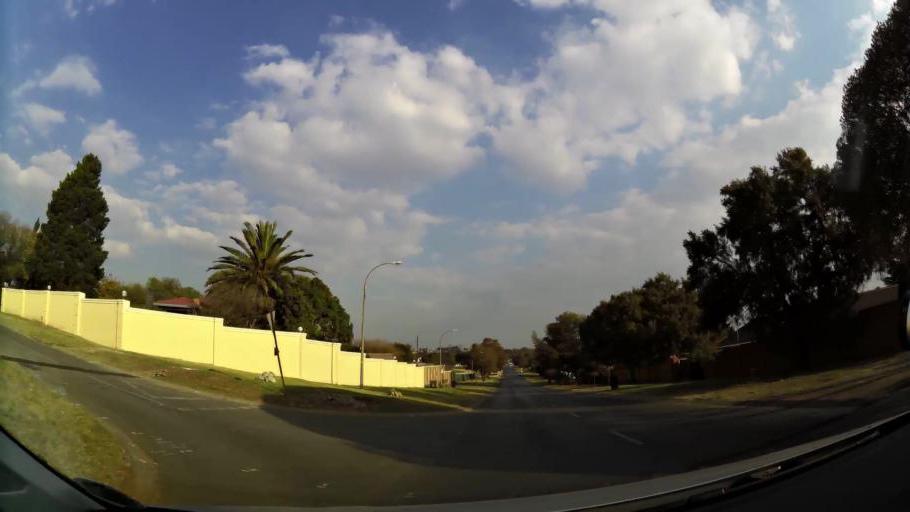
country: ZA
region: Gauteng
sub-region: City of Johannesburg Metropolitan Municipality
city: Modderfontein
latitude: -26.1277
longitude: 28.1932
